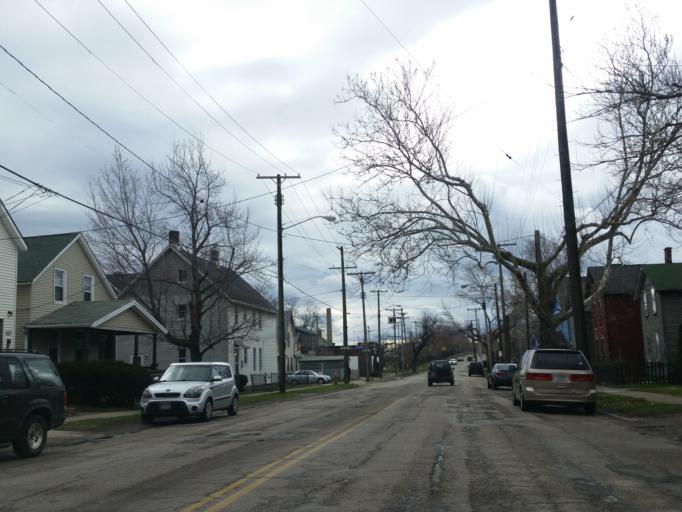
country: US
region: Ohio
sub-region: Cuyahoga County
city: Cleveland
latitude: 41.4792
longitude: -81.7099
